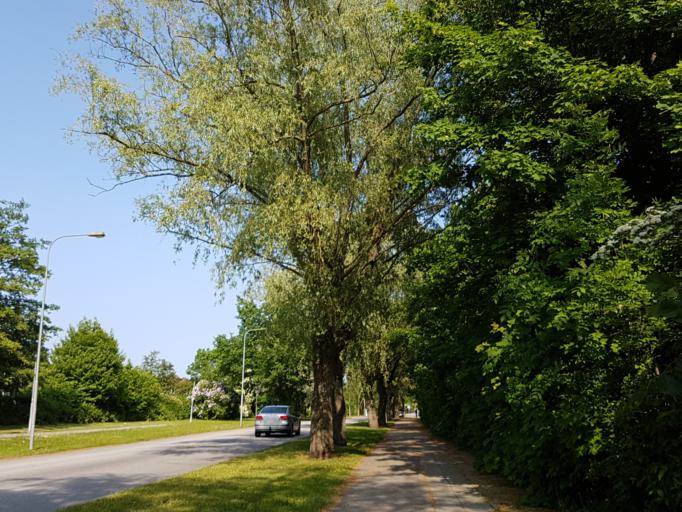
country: SE
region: Skane
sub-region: Lunds Kommun
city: Lund
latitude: 55.6999
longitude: 13.2260
